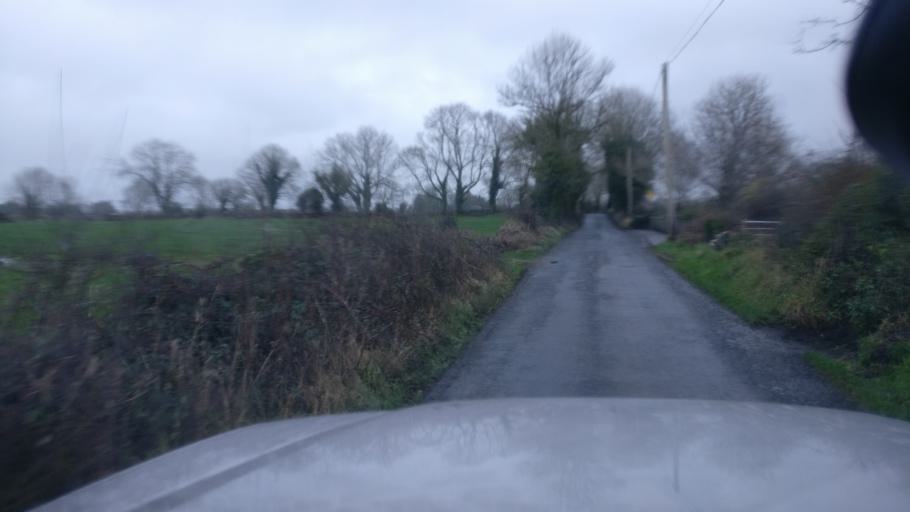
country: IE
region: Connaught
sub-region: County Galway
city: Loughrea
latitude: 53.2281
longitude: -8.6268
